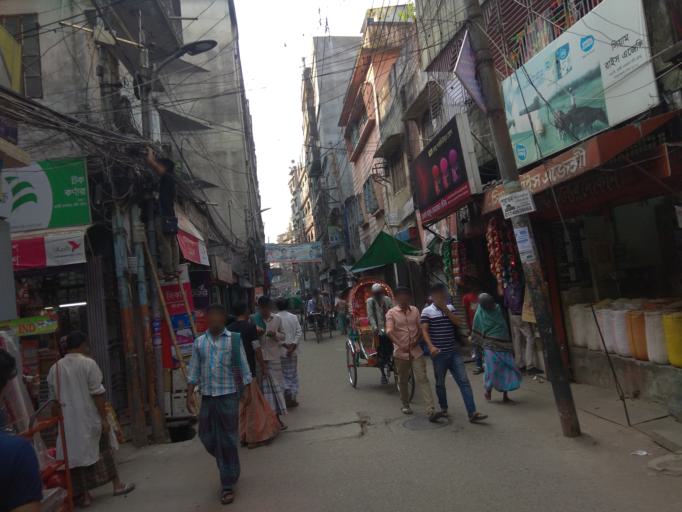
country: BD
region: Dhaka
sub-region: Dhaka
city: Dhaka
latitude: 23.7202
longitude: 90.4088
